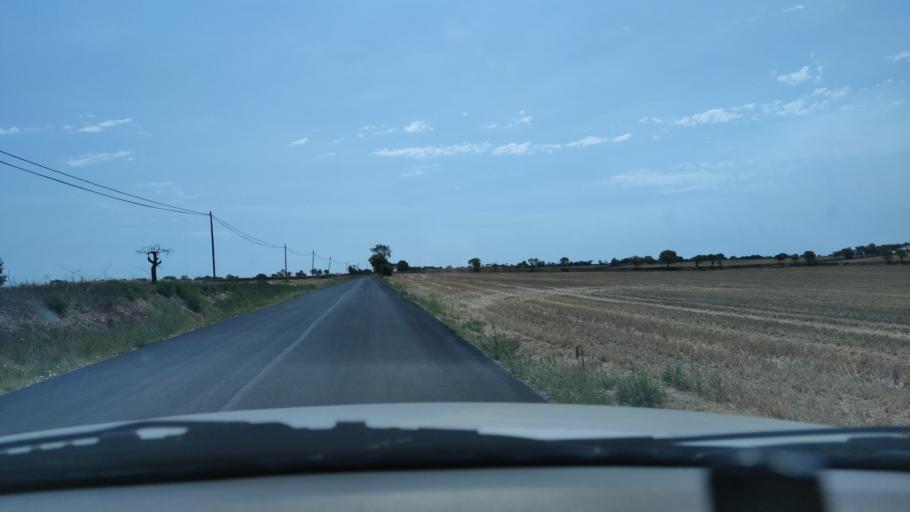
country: ES
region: Catalonia
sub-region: Provincia de Lleida
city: Ivorra
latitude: 41.7803
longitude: 1.3077
